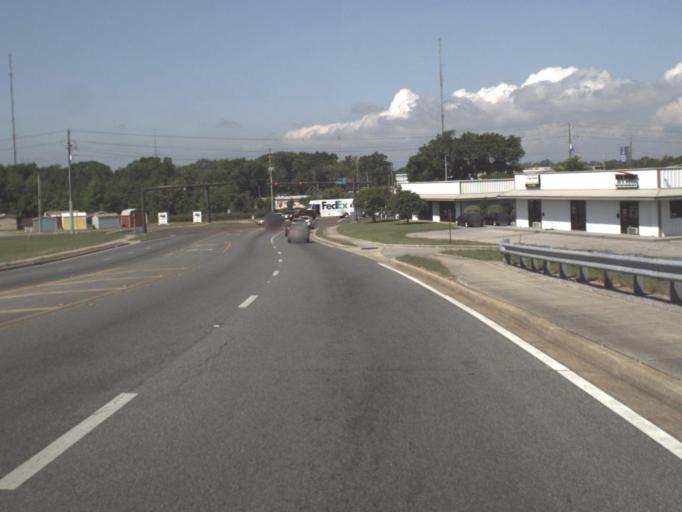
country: US
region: Florida
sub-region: Escambia County
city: Goulding
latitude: 30.4456
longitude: -87.2258
